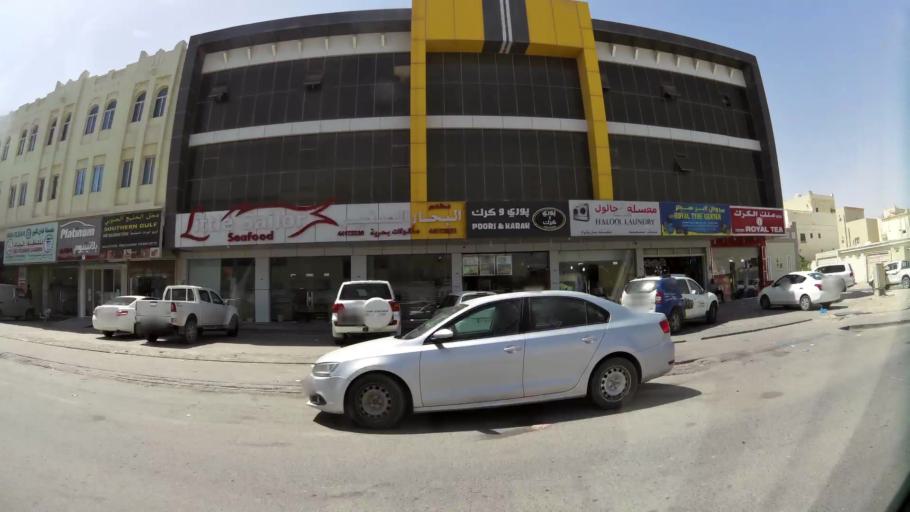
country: QA
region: Baladiyat ar Rayyan
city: Ar Rayyan
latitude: 25.2792
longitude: 51.4078
